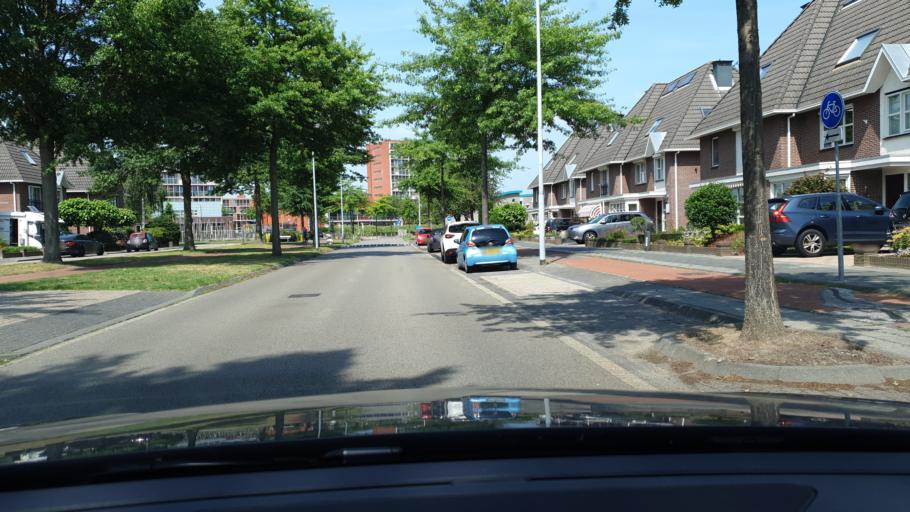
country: NL
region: North Brabant
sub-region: Gemeente Son en Breugel
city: Son
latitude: 51.4865
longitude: 5.4741
